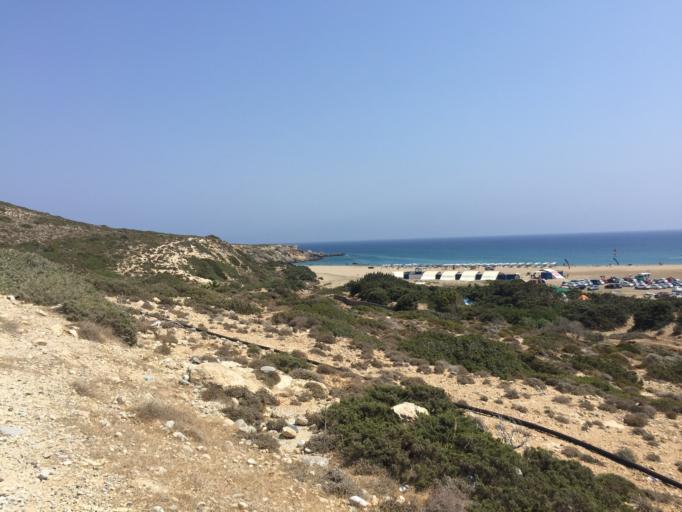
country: GR
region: South Aegean
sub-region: Nomos Dodekanisou
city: Lardos
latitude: 35.8916
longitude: 27.7752
